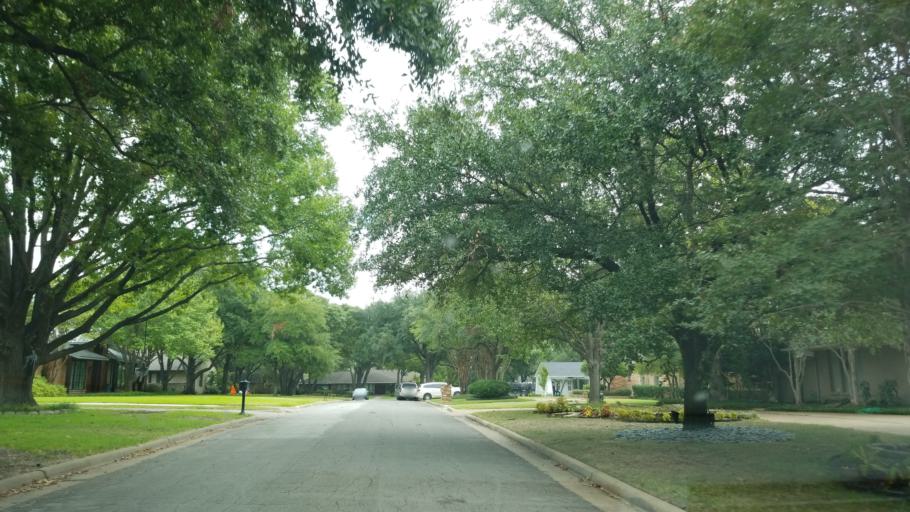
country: US
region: Texas
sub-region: Dallas County
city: Richardson
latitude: 32.9431
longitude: -96.7744
